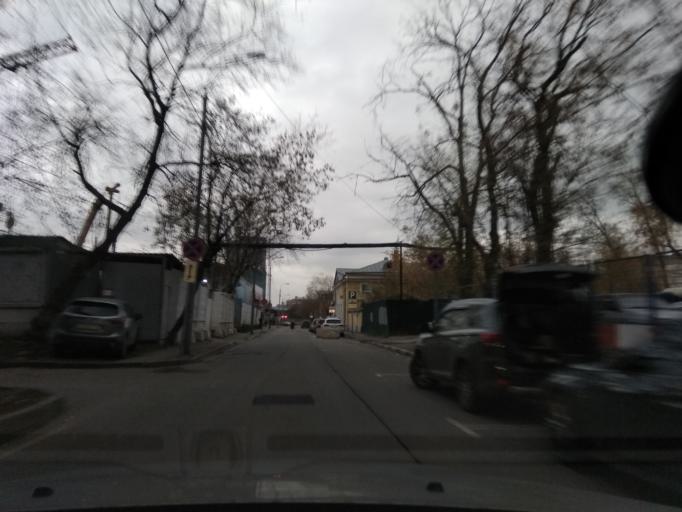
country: RU
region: Moscow
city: Mar'ina Roshcha
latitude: 55.7935
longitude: 37.5956
